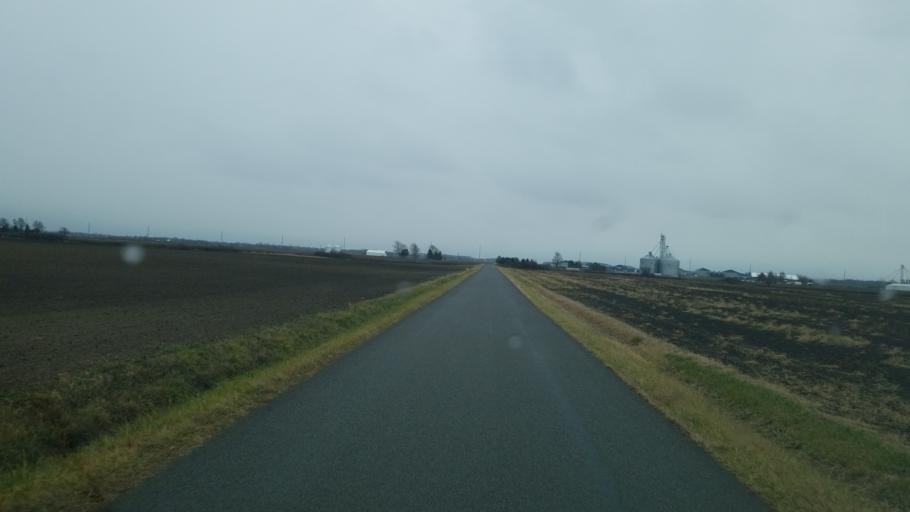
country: US
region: Ohio
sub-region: Logan County
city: Northwood
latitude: 40.4406
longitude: -83.5646
